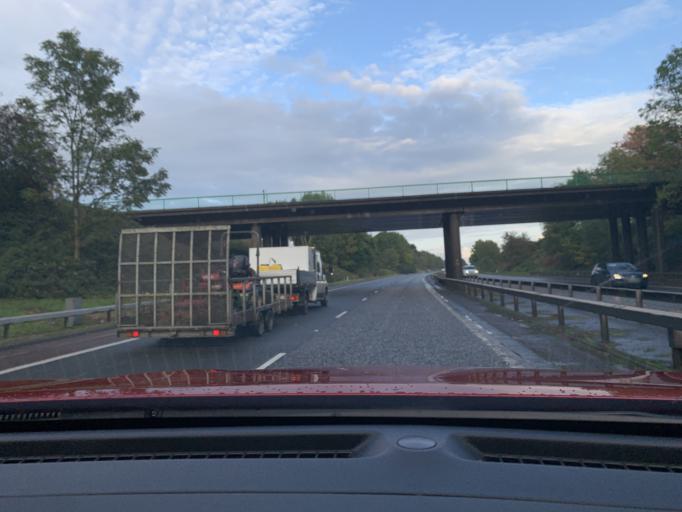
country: GB
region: Northern Ireland
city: Coalisland
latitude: 54.4942
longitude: -6.7054
